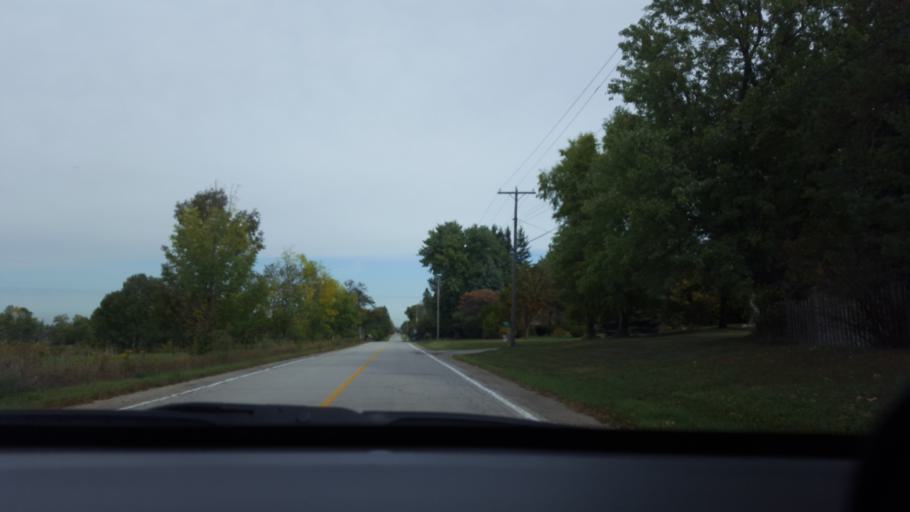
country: CA
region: Ontario
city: Newmarket
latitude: 44.0163
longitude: -79.5512
